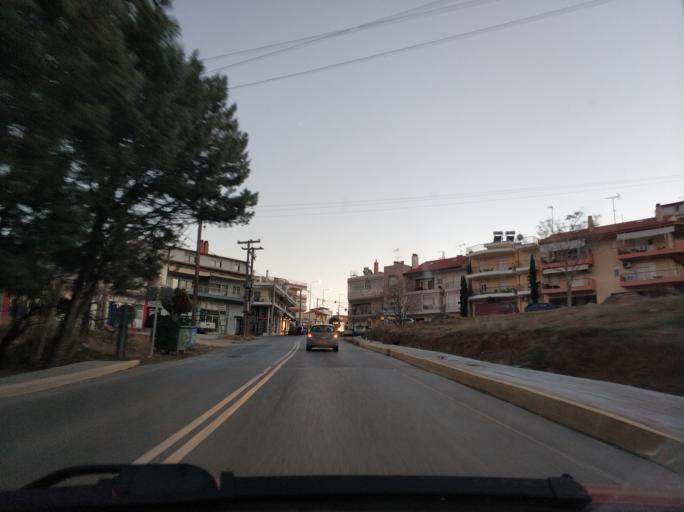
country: GR
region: Central Macedonia
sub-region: Nomos Thessalonikis
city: Polichni
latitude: 40.6709
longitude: 22.9454
